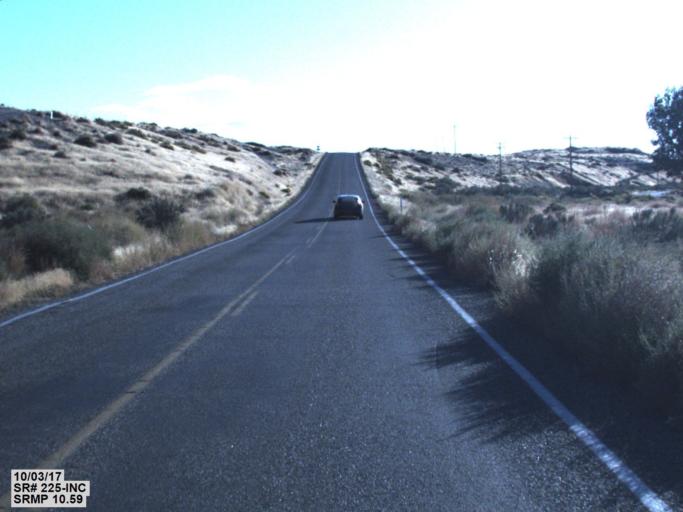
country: US
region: Washington
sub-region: Benton County
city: West Richland
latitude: 46.3815
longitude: -119.4378
